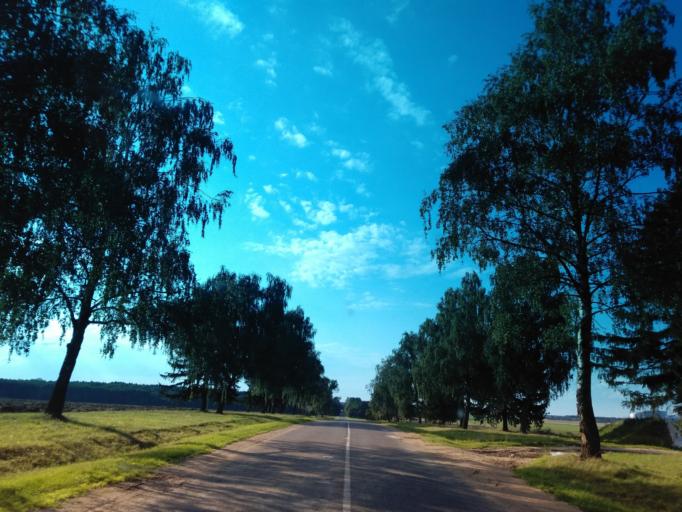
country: BY
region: Minsk
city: Kapyl'
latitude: 53.2072
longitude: 27.0279
